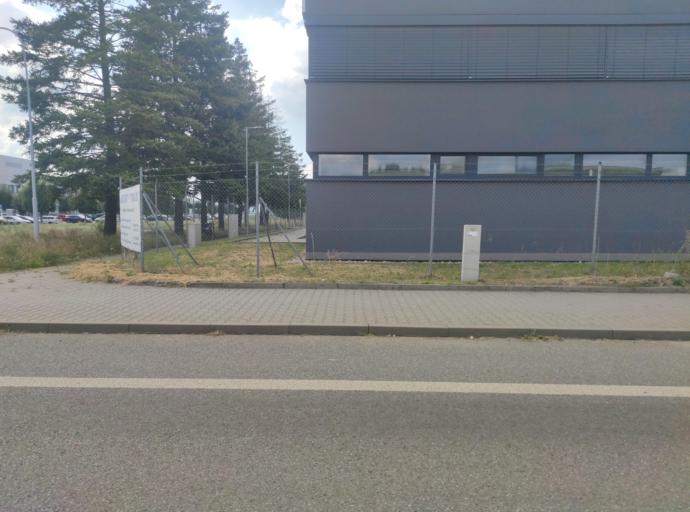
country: CZ
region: South Moravian
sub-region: Mesto Brno
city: Brno
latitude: 49.1841
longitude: 16.6571
